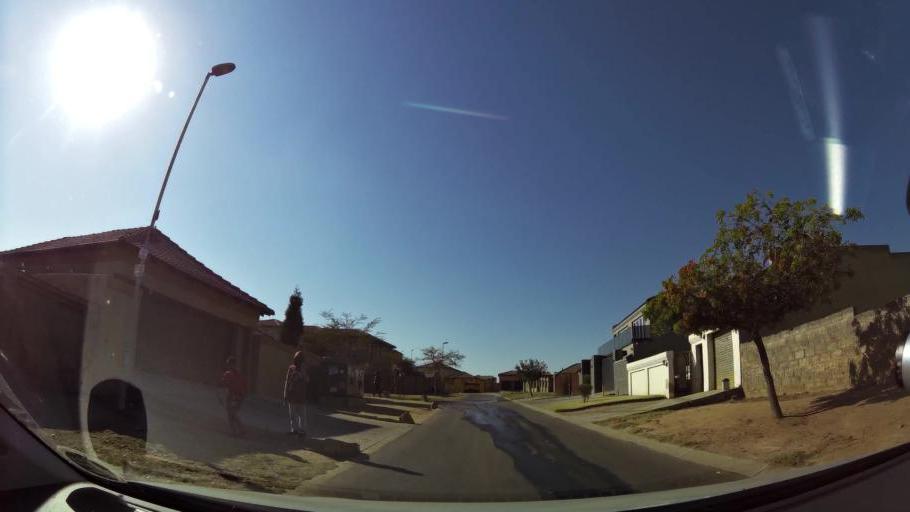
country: ZA
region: Gauteng
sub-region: City of Johannesburg Metropolitan Municipality
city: Modderfontein
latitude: -26.0455
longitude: 28.1990
